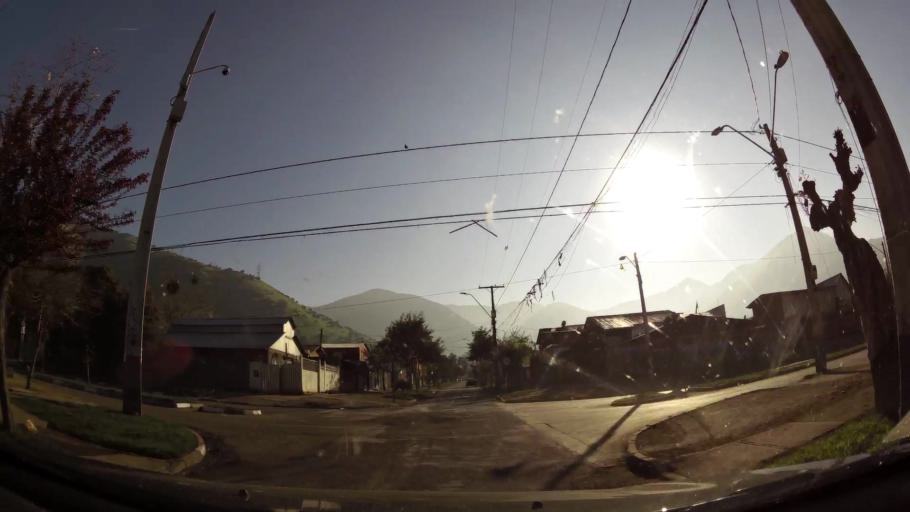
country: CL
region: Santiago Metropolitan
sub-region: Provincia de Chacabuco
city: Chicureo Abajo
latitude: -33.3629
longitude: -70.6360
